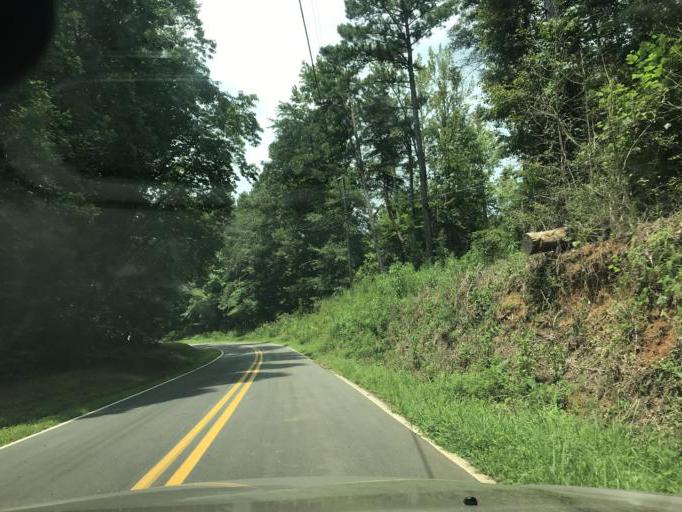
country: US
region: Georgia
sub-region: Dawson County
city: Dawsonville
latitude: 34.3301
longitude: -84.2077
